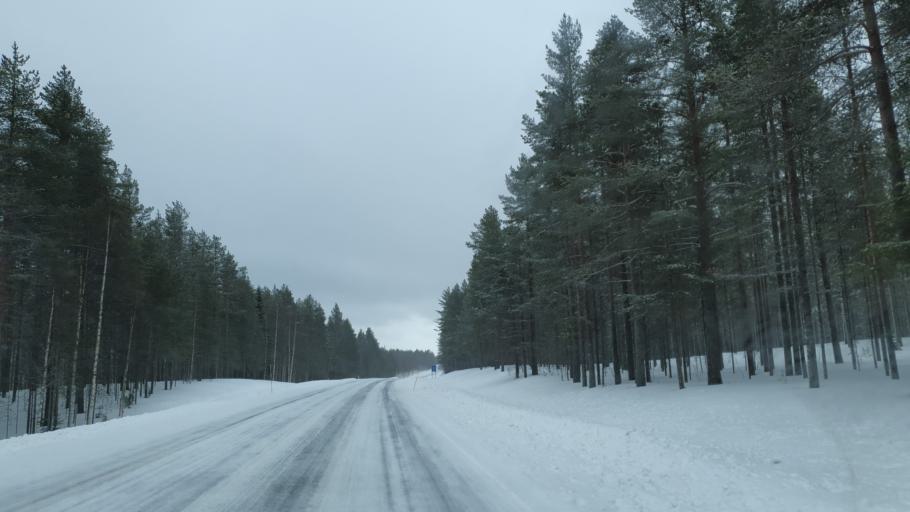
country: FI
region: Lapland
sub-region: Rovaniemi
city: Ranua
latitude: 66.1724
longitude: 26.2344
